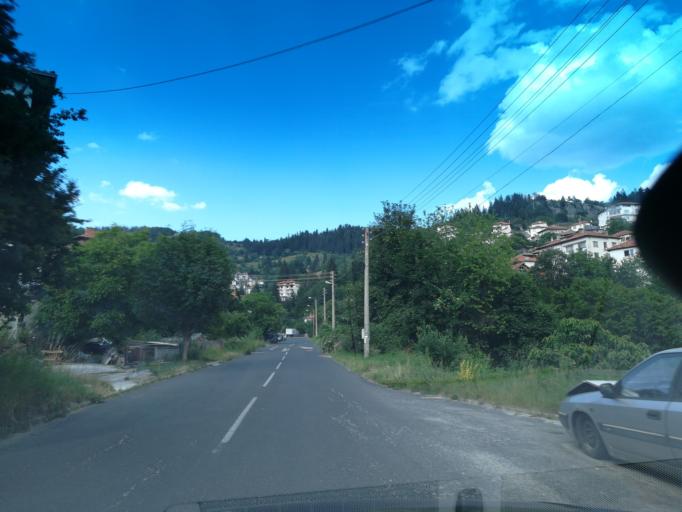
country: BG
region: Smolyan
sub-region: Obshtina Smolyan
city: Smolyan
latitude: 41.6573
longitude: 24.7747
